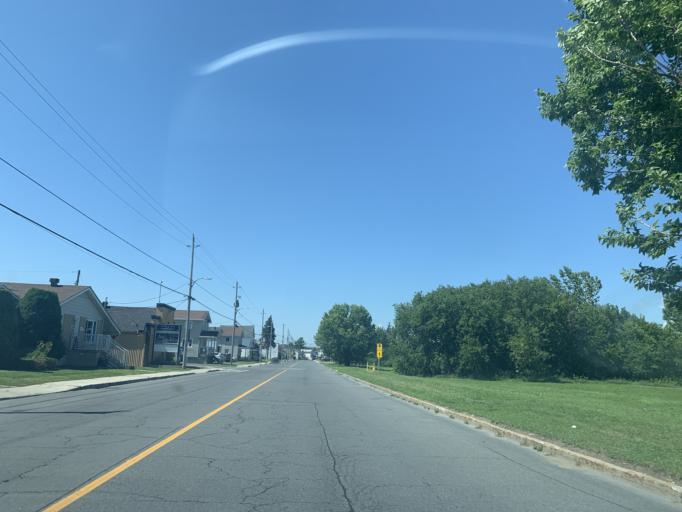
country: CA
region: Ontario
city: Hawkesbury
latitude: 45.6076
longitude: -74.5857
